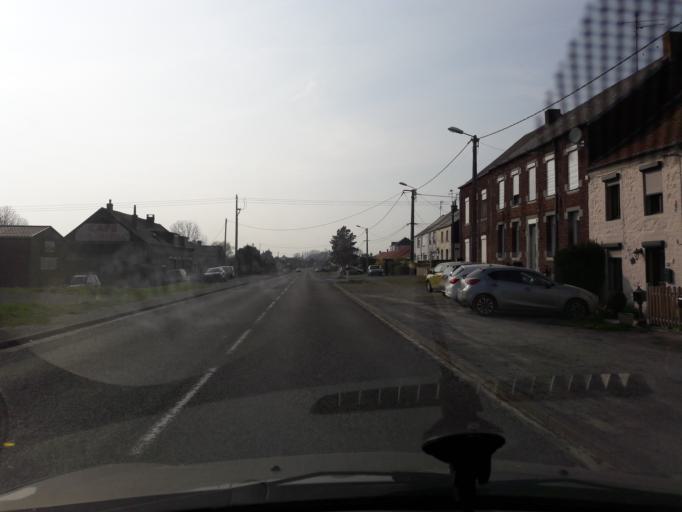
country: FR
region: Nord-Pas-de-Calais
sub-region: Departement du Nord
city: Recquignies
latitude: 50.2590
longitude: 4.0339
